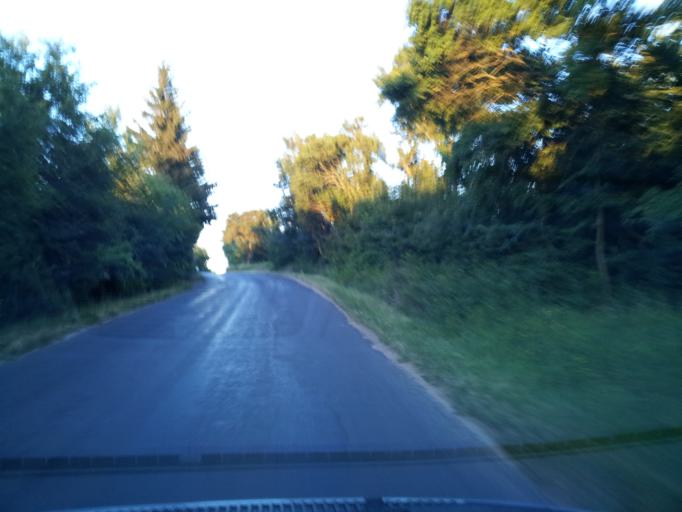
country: HU
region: Veszprem
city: Szentkiralyszabadja
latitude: 47.0149
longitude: 17.9744
